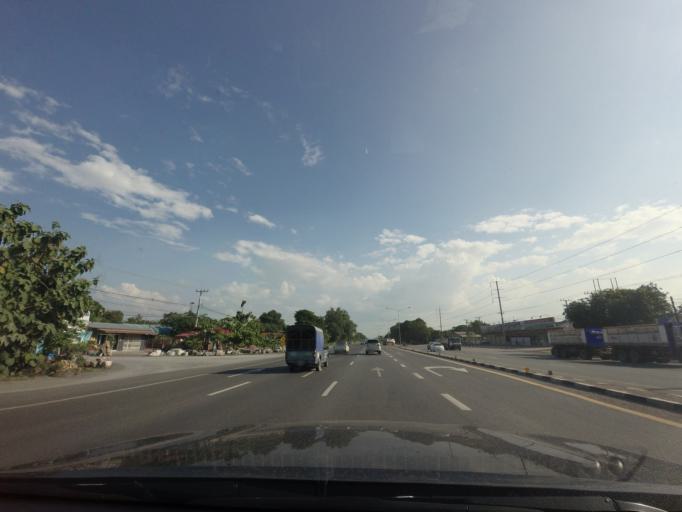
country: TH
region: Sara Buri
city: Chaloem Phra Kiat
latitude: 14.6423
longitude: 100.8865
